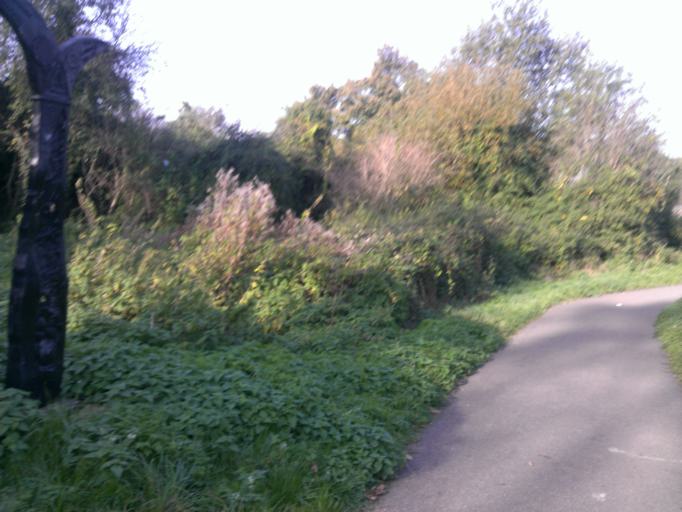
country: GB
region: England
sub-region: Essex
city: Colchester
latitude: 51.8871
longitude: 0.9175
